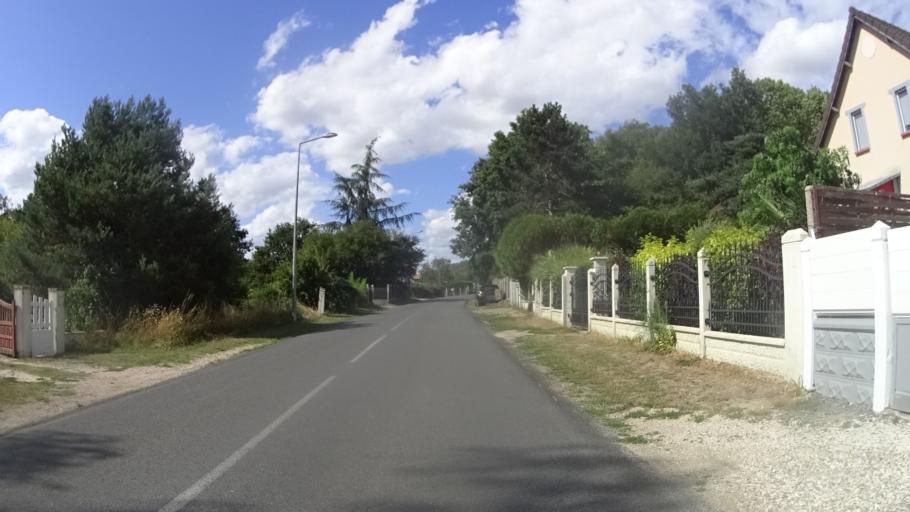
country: FR
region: Ile-de-France
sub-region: Departement de l'Essonne
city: Boutigny-sur-Essonne
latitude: 48.4497
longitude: 2.3667
